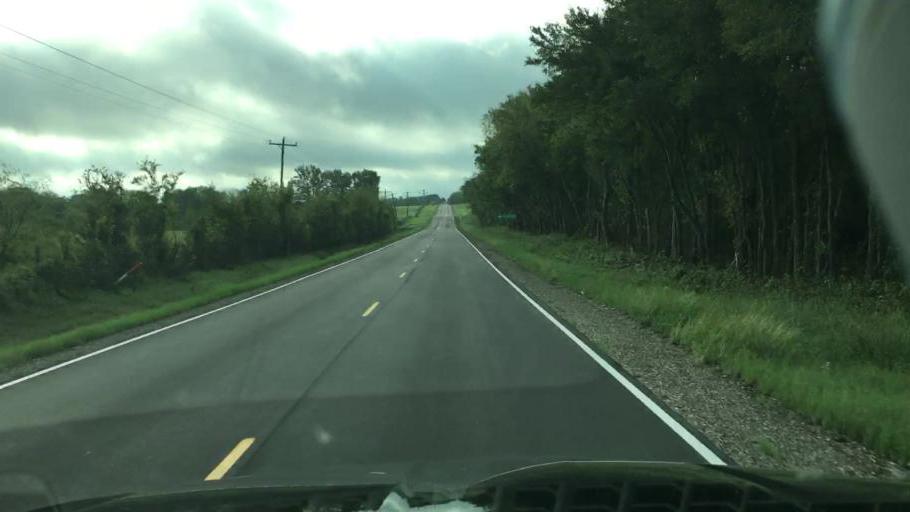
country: US
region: Texas
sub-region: Lee County
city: Lexington
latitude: 30.3706
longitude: -96.8419
